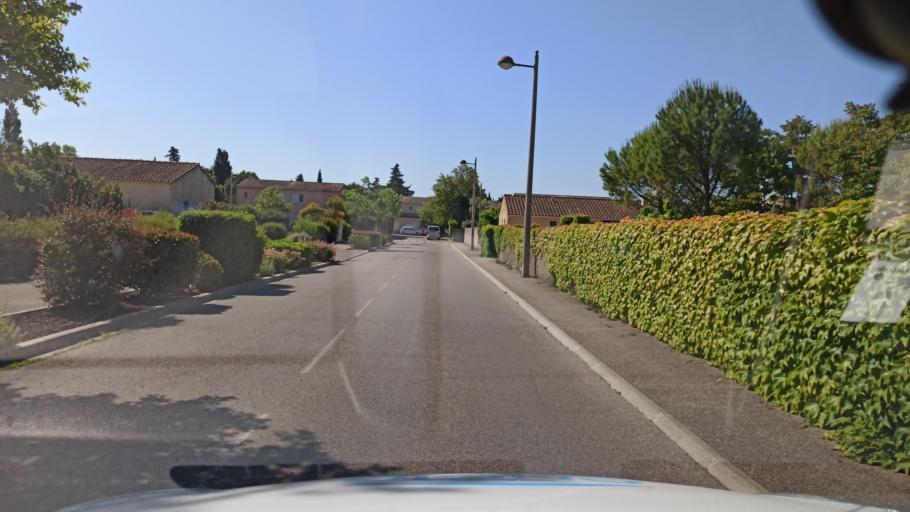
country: FR
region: Provence-Alpes-Cote d'Azur
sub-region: Departement du Vaucluse
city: Monteux
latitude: 44.0336
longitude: 5.0027
